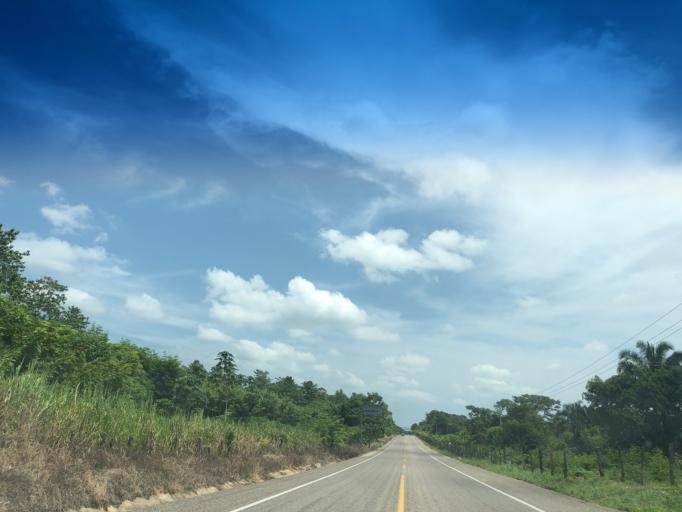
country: MX
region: Tabasco
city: Chontalpa
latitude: 17.5981
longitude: -93.5282
